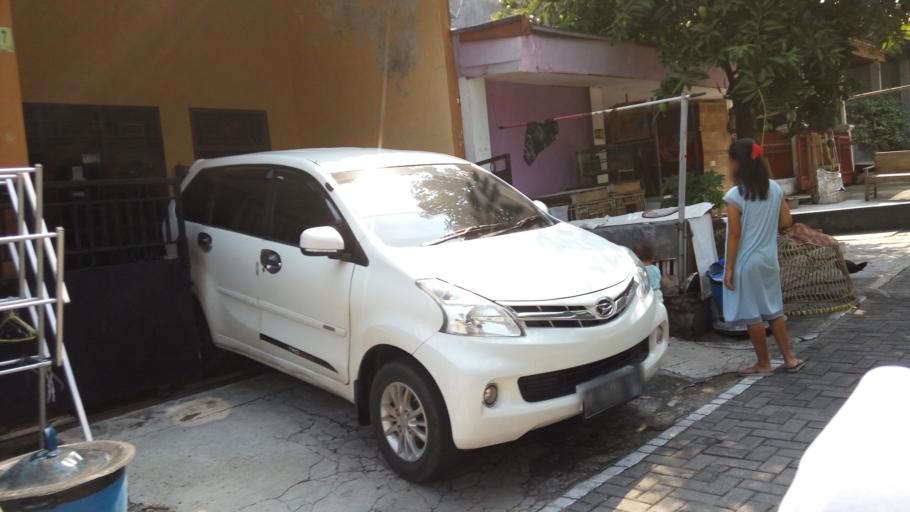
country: ID
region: Central Java
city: Mranggen
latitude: -7.0340
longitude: 110.4731
